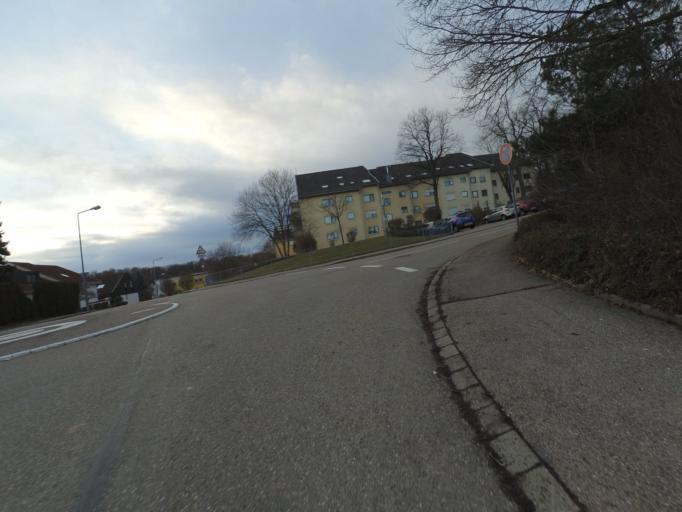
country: DE
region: Baden-Wuerttemberg
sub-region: Regierungsbezirk Stuttgart
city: Aalen
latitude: 48.8434
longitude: 10.0847
